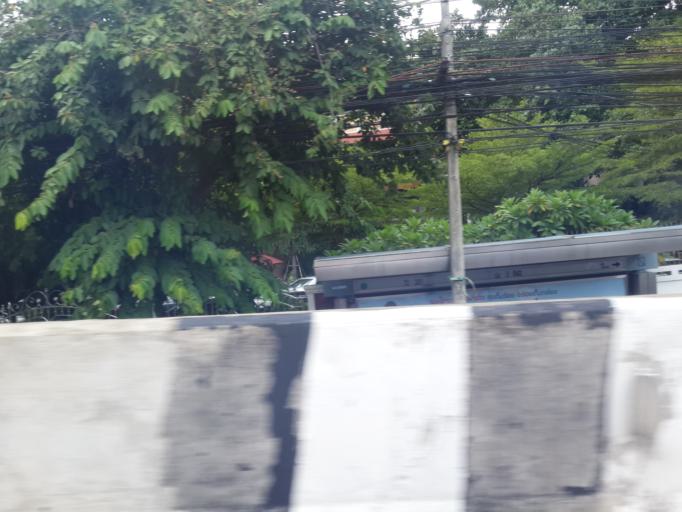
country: TH
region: Bangkok
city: Ratchathewi
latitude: 13.7588
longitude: 100.5322
